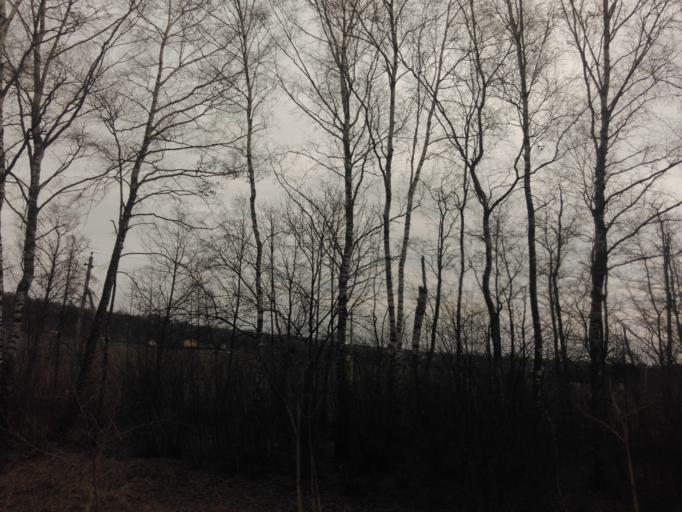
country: RU
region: Moskovskaya
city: Tuchkovo
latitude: 55.6133
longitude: 36.5023
